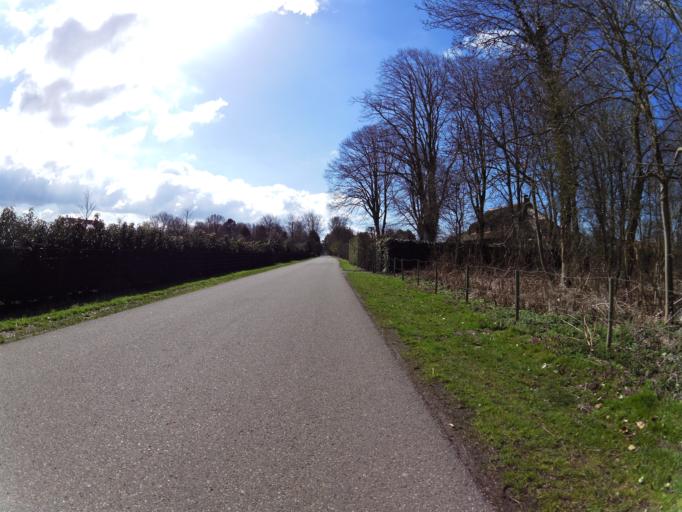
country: NL
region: South Holland
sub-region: Gemeente Hellevoetsluis
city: Nieuw-Helvoet
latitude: 51.8943
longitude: 4.0749
